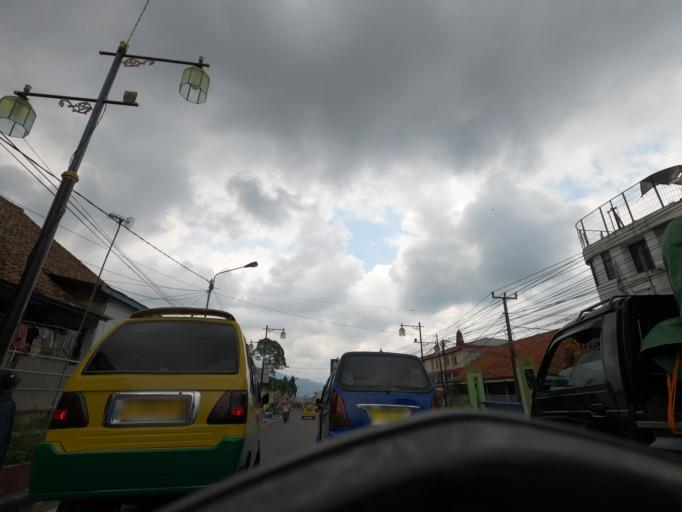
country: ID
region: West Java
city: Sukabumi
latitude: -6.7391
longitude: 107.0447
